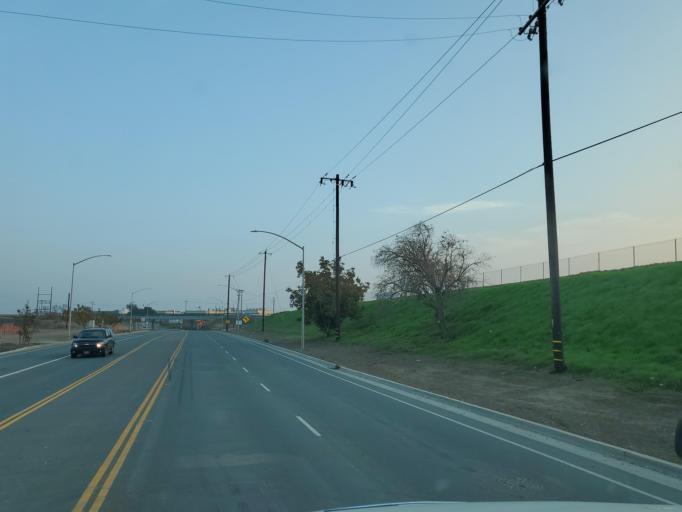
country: US
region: California
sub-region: San Joaquin County
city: Country Club
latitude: 37.9396
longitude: -121.3318
